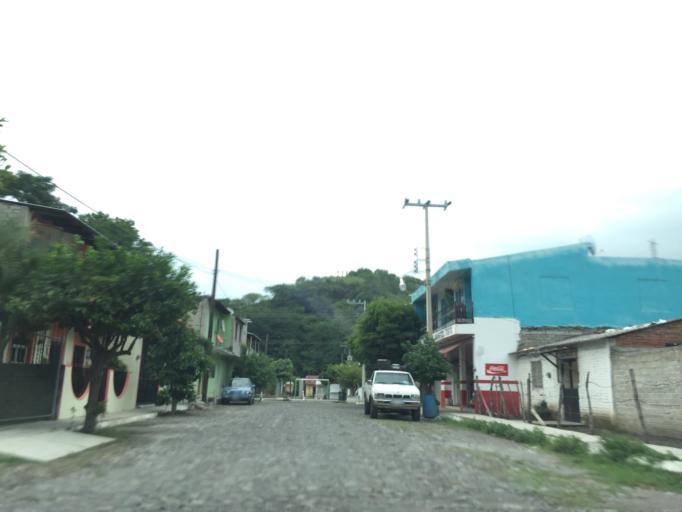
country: MX
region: Colima
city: Comala
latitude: 19.3707
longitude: -103.7989
